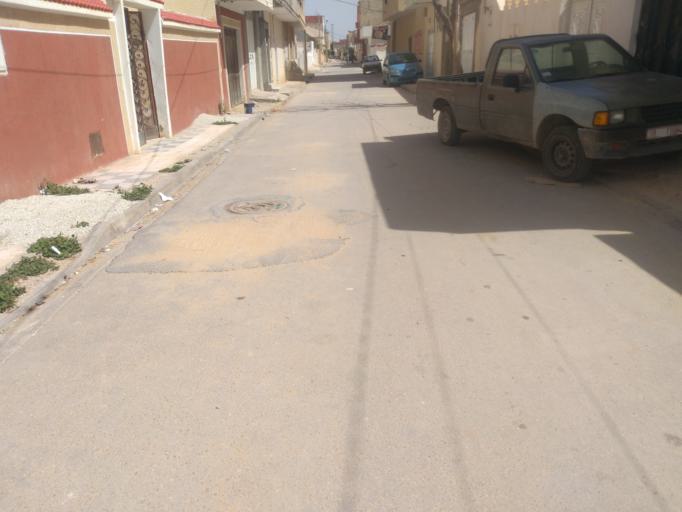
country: TN
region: Al Qayrawan
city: Kairouan
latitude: 35.6654
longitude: 10.0793
